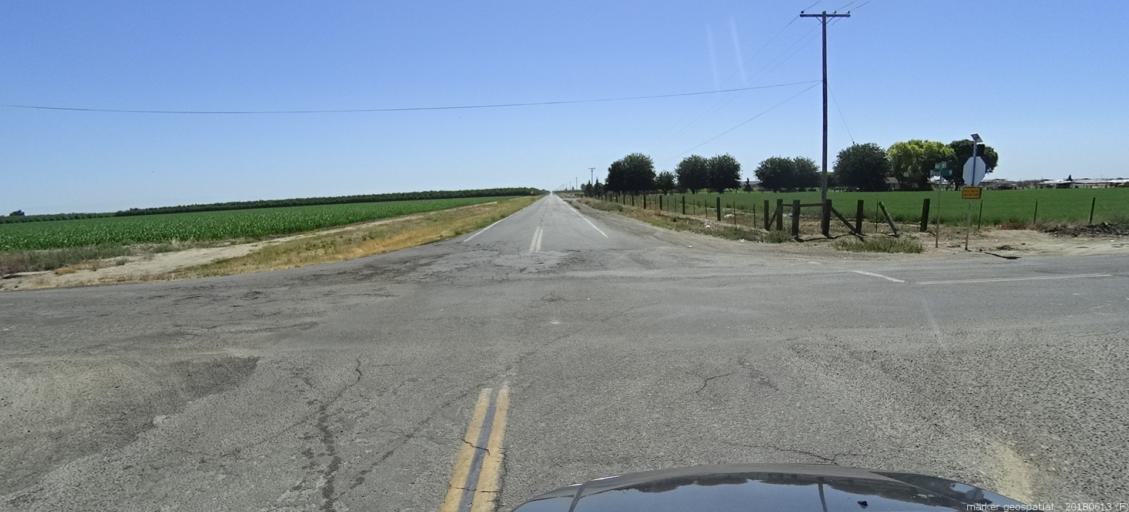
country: US
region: California
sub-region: Madera County
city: Chowchilla
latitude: 37.0180
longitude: -120.3835
